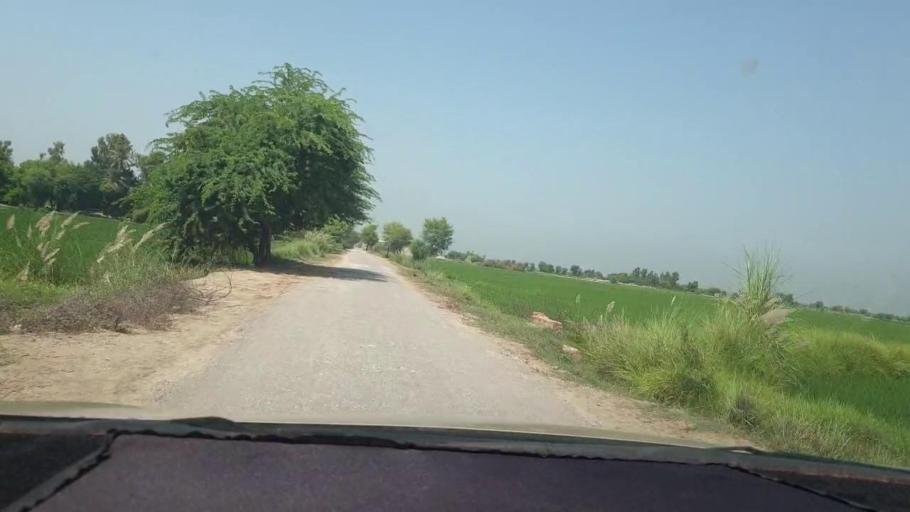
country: PK
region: Sindh
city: Kambar
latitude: 27.6117
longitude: 68.0597
